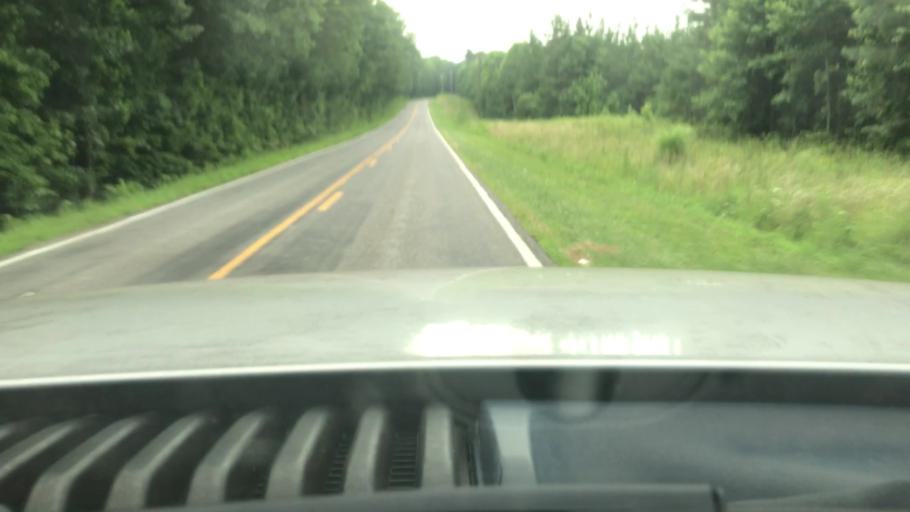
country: US
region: North Carolina
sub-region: Surry County
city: Dobson
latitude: 36.4133
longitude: -80.8192
